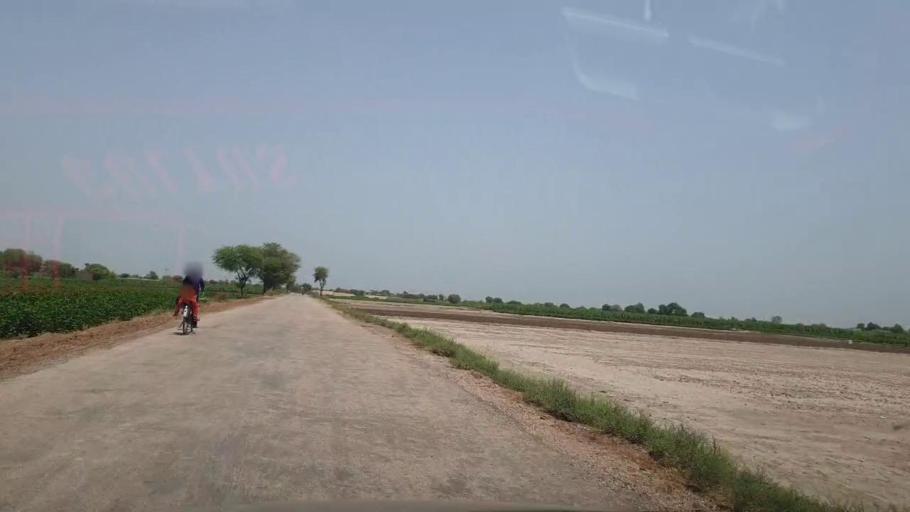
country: PK
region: Sindh
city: Daulatpur
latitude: 26.3880
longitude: 68.0525
